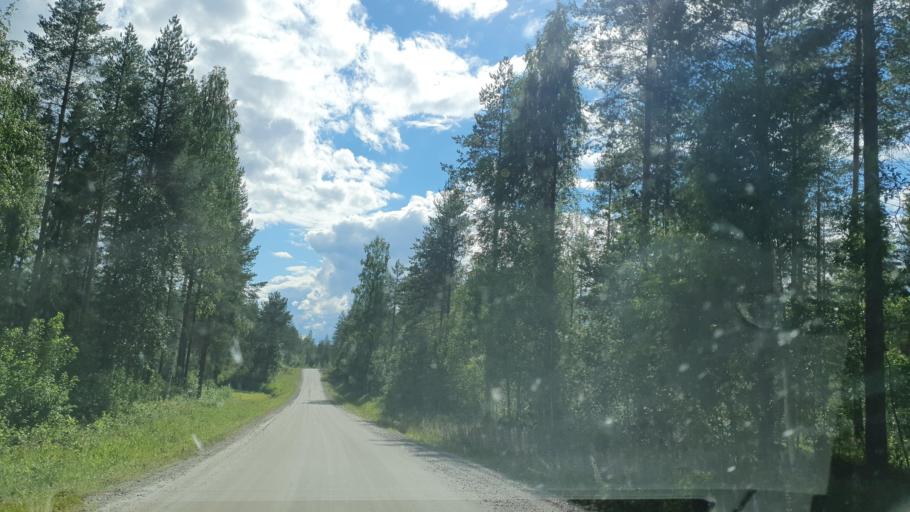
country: FI
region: Kainuu
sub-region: Kehys-Kainuu
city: Kuhmo
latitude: 64.1393
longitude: 29.6830
